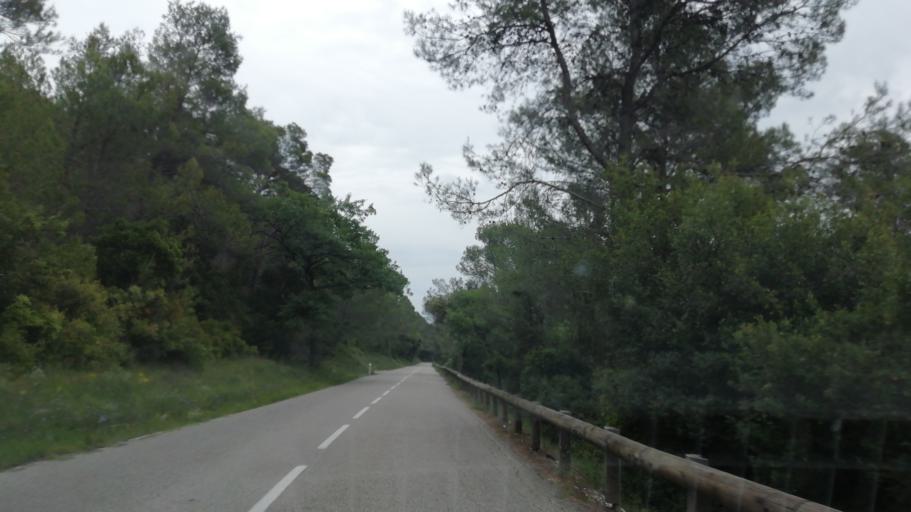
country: FR
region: Languedoc-Roussillon
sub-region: Departement de l'Herault
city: Saint-Mathieu-de-Treviers
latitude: 43.7910
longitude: 3.8129
